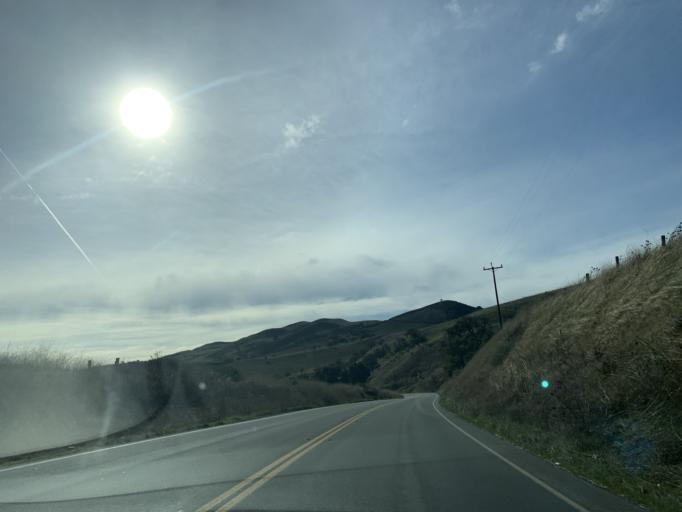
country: US
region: California
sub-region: San Benito County
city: Ridgemark
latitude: 36.7590
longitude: -121.2955
